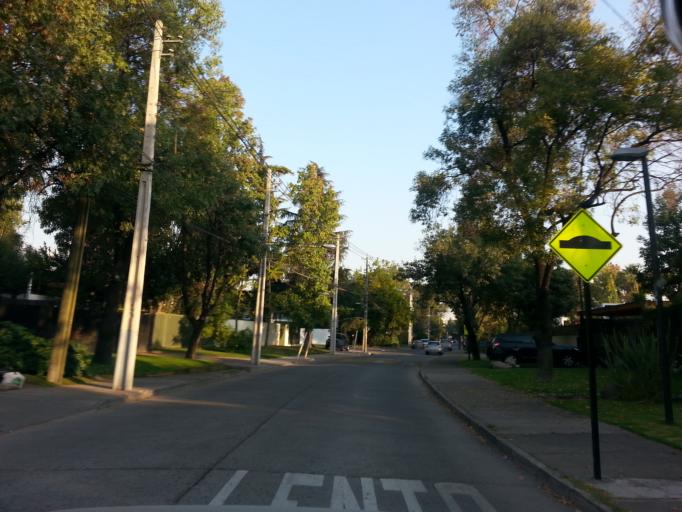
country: CL
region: Santiago Metropolitan
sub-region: Provincia de Santiago
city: Villa Presidente Frei, Nunoa, Santiago, Chile
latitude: -33.3817
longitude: -70.5740
